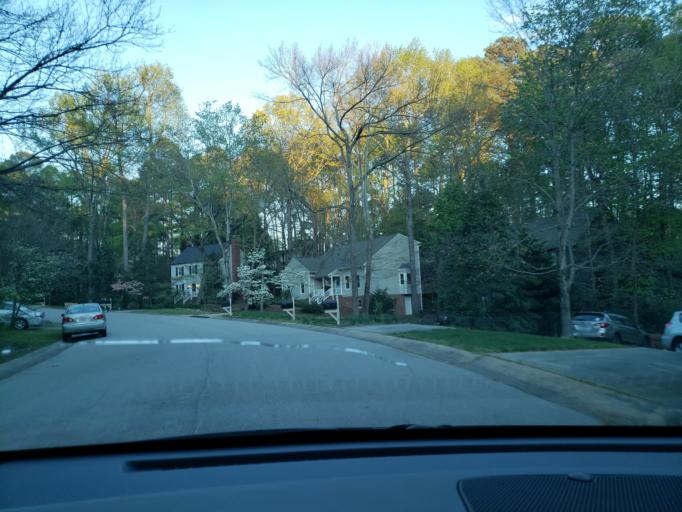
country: US
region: North Carolina
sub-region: Durham County
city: Durham
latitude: 35.9199
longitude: -78.9468
